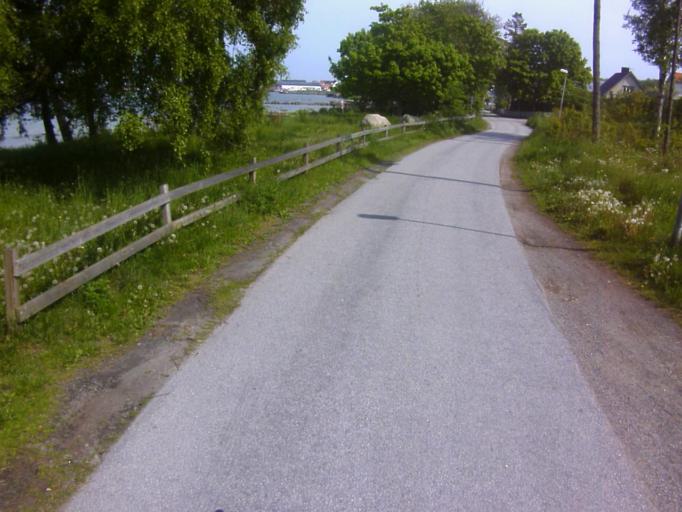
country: SE
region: Blekinge
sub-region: Karlshamns Kommun
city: Morrum
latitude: 56.0425
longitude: 14.7597
